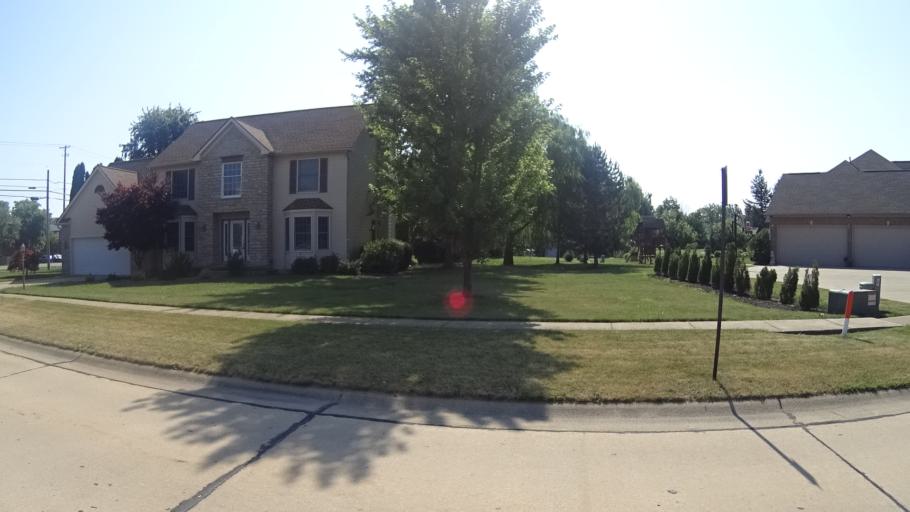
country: US
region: Ohio
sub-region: Erie County
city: Huron
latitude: 41.4071
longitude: -82.5743
